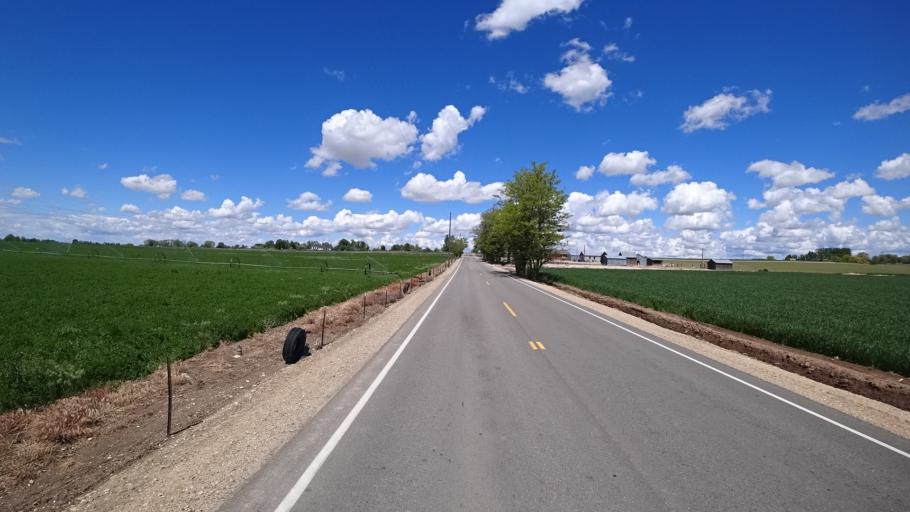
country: US
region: Idaho
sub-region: Ada County
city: Kuna
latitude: 43.5633
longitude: -116.4536
